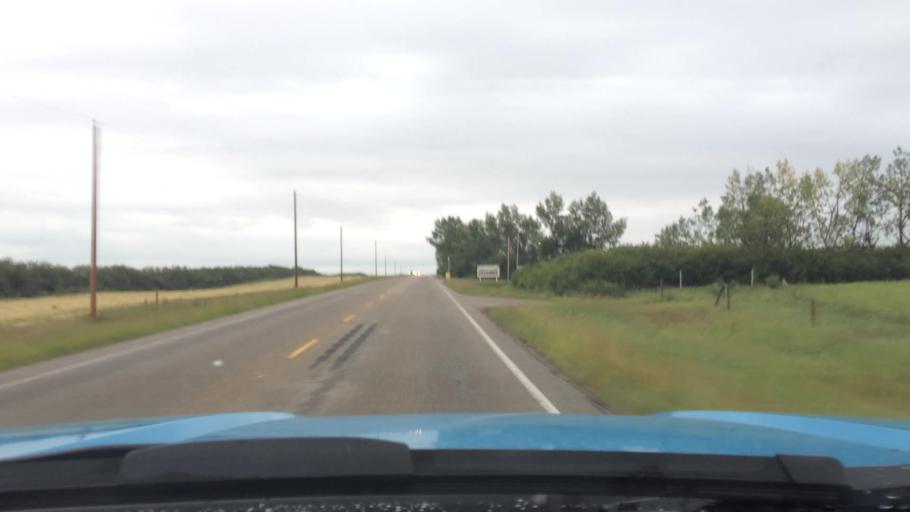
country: CA
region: Alberta
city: Airdrie
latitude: 51.2124
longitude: -114.0615
